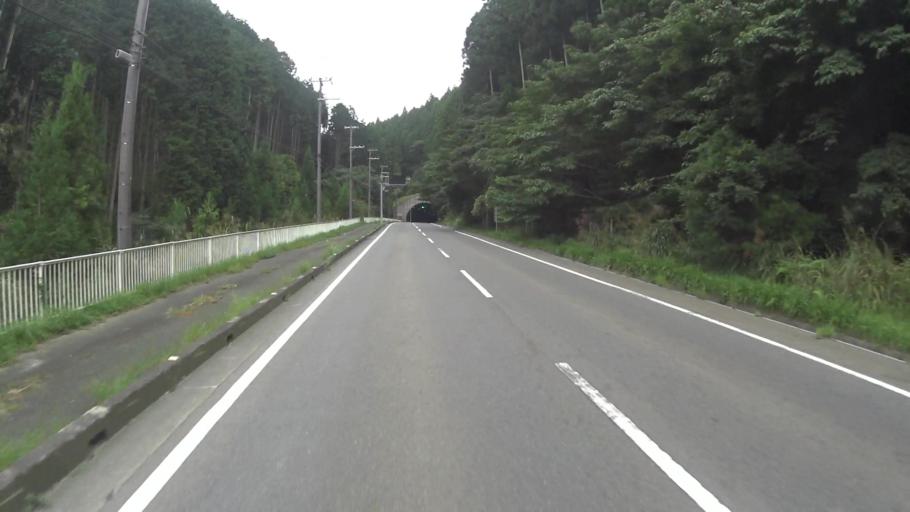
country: JP
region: Kyoto
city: Uji
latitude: 34.8556
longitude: 135.9590
